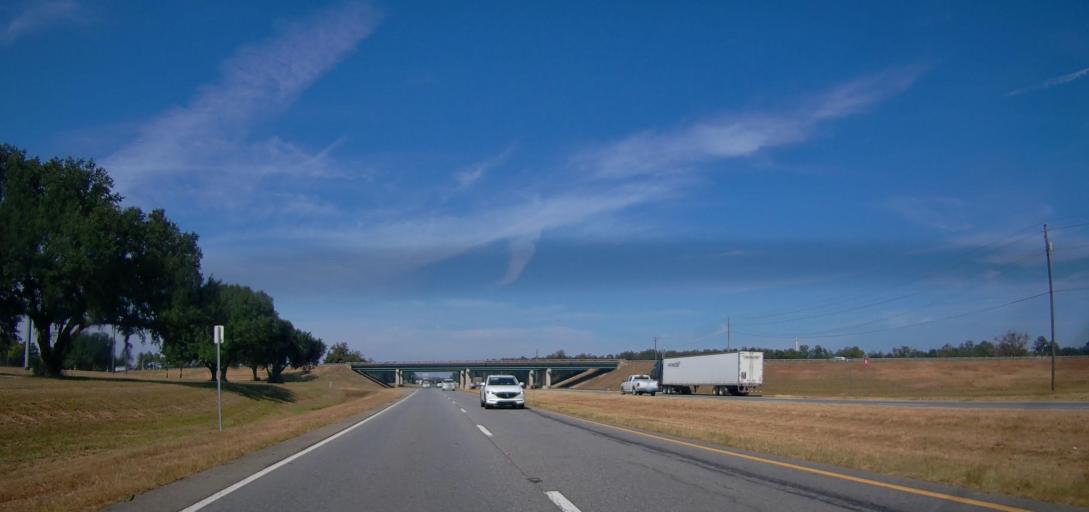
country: US
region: Georgia
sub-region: Dougherty County
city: Albany
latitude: 31.5440
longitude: -84.1152
